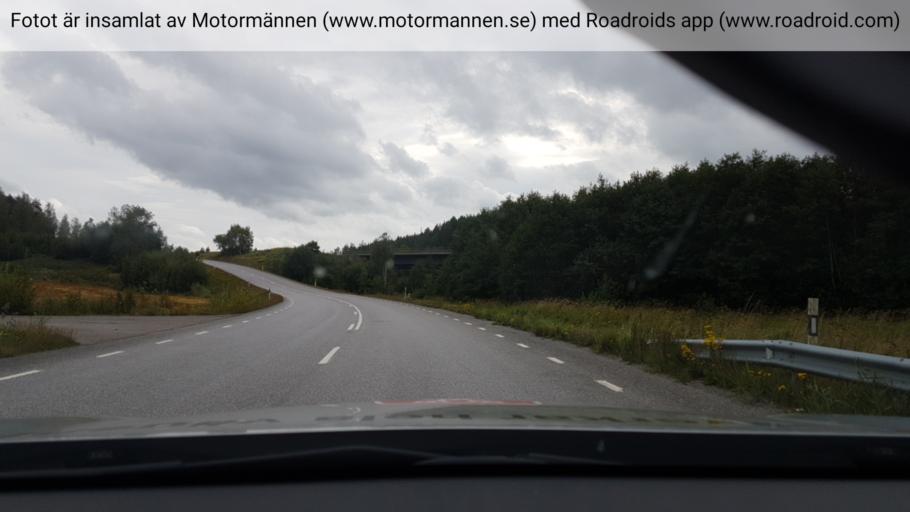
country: SE
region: Vaestra Goetaland
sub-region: Munkedals Kommun
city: Munkedal
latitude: 58.4976
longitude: 11.5733
